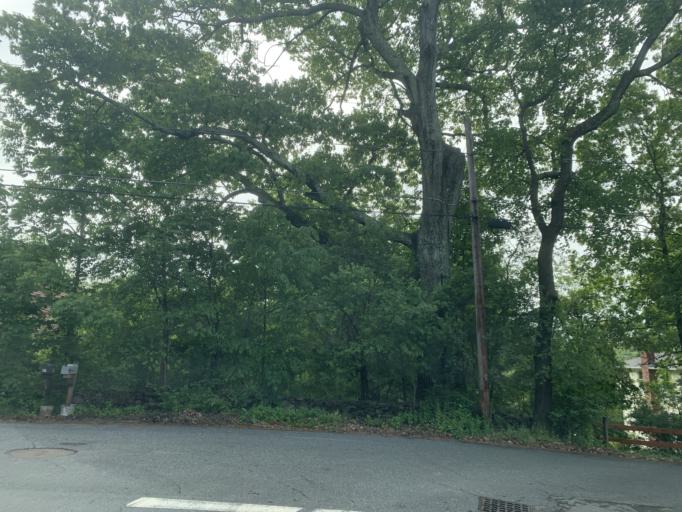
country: US
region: Massachusetts
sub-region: Worcester County
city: Grafton
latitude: 42.2007
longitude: -71.6489
